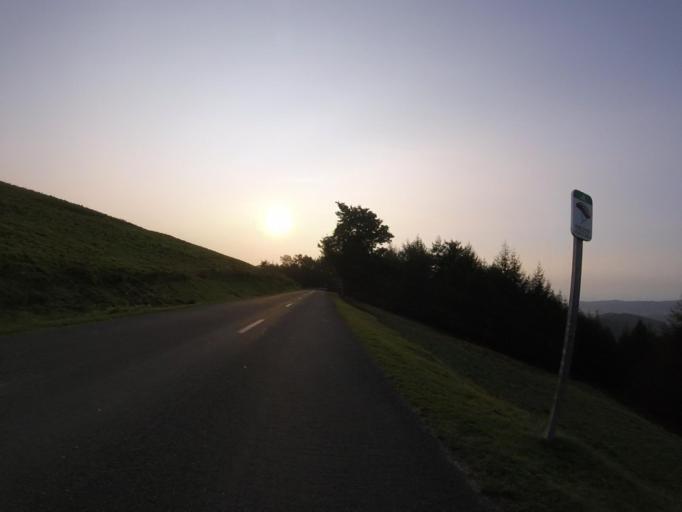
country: ES
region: Navarre
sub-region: Provincia de Navarra
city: Arano
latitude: 43.2443
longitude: -1.8338
